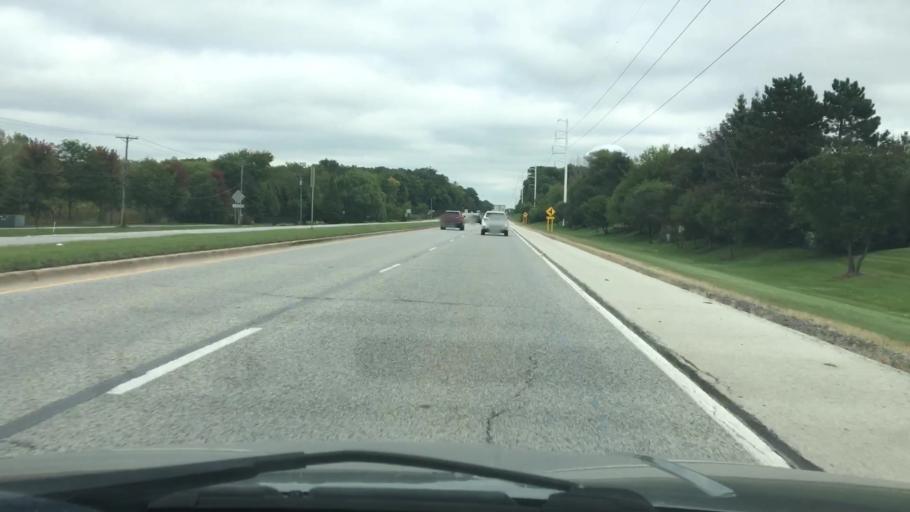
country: US
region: Illinois
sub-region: DuPage County
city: Woodridge
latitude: 41.7492
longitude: -88.0929
